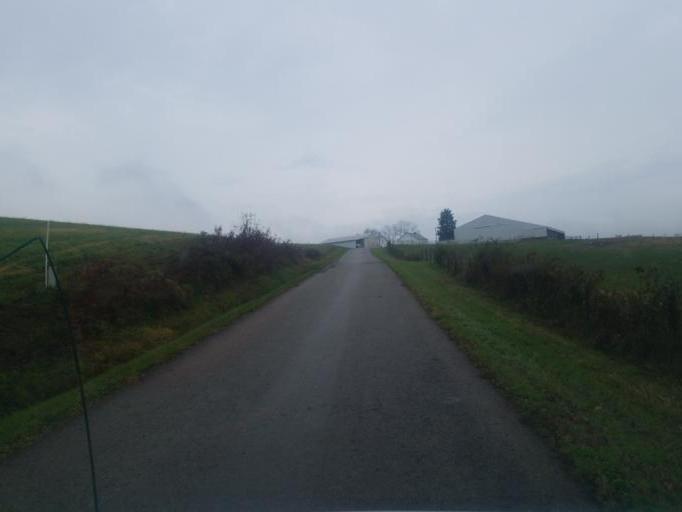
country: US
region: Ohio
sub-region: Morgan County
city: McConnelsville
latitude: 39.5055
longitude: -81.8015
